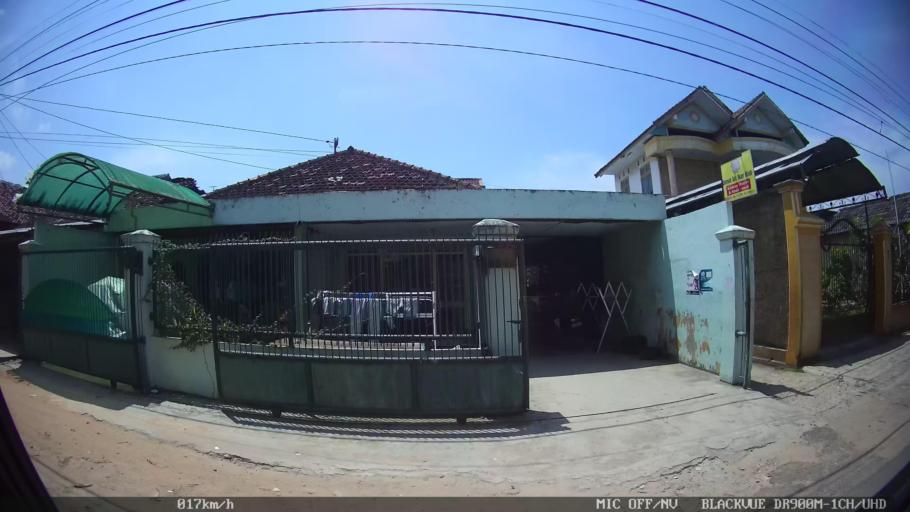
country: ID
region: Lampung
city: Bandarlampung
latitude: -5.4057
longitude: 105.2675
